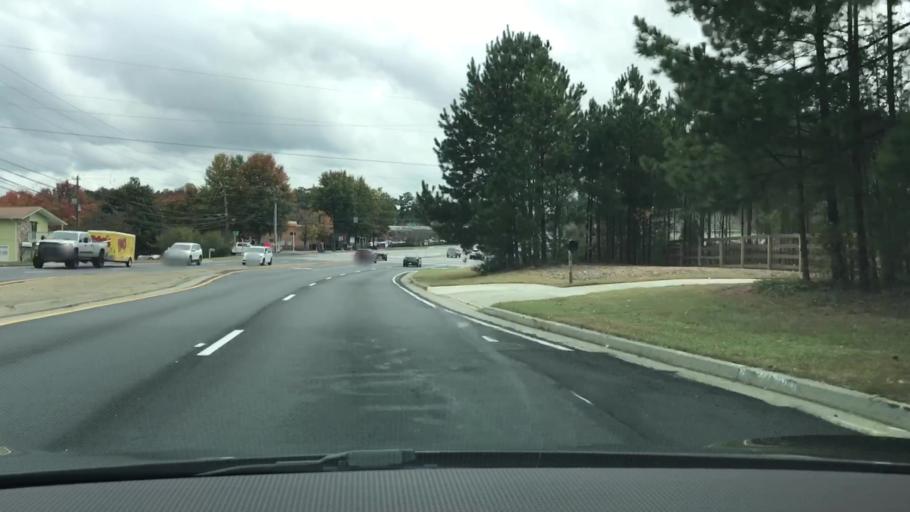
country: US
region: Georgia
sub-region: Gwinnett County
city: Suwanee
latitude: 34.0056
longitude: -84.0412
